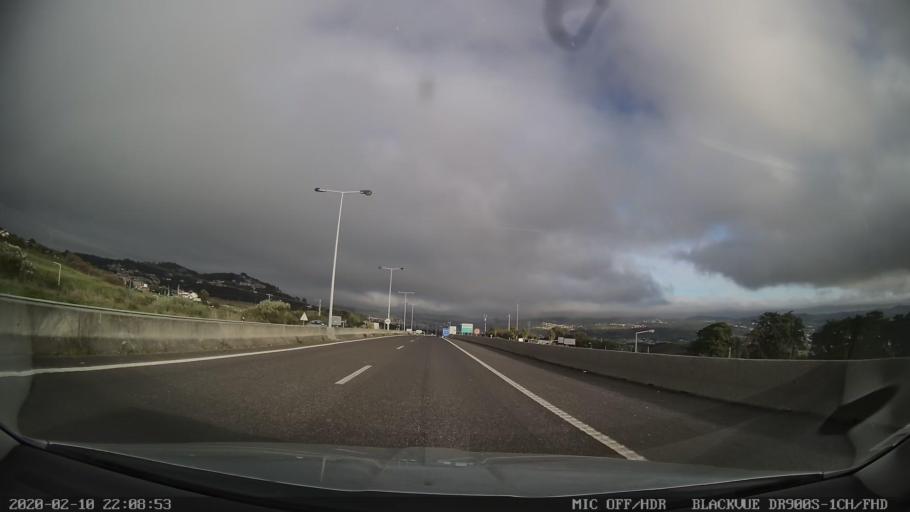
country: PT
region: Lisbon
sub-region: Odivelas
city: Ramada
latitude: 38.8143
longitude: -9.1840
